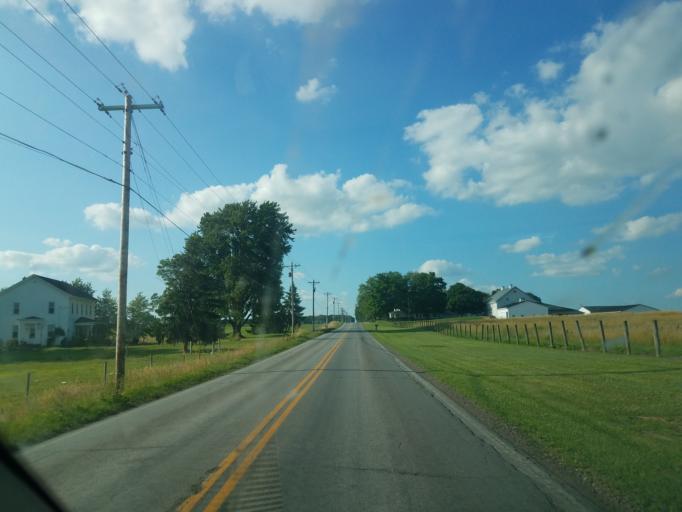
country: US
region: Ohio
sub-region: Wayne County
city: Apple Creek
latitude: 40.7294
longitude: -81.8966
